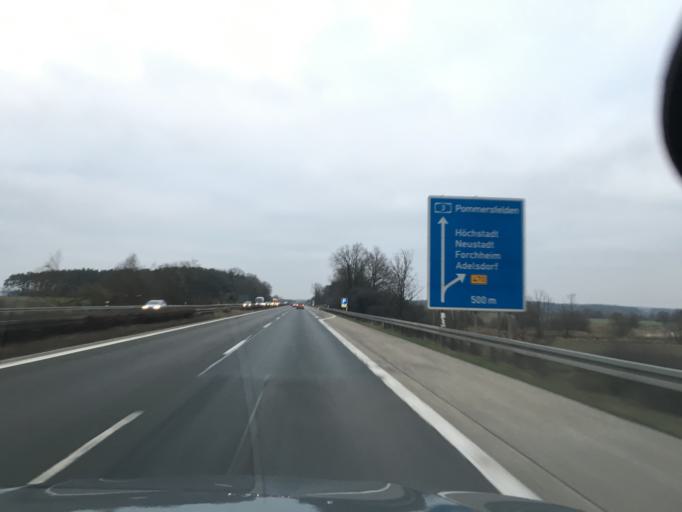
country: DE
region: Bavaria
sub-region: Regierungsbezirk Mittelfranken
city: Gremsdorf
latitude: 49.6926
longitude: 10.8589
